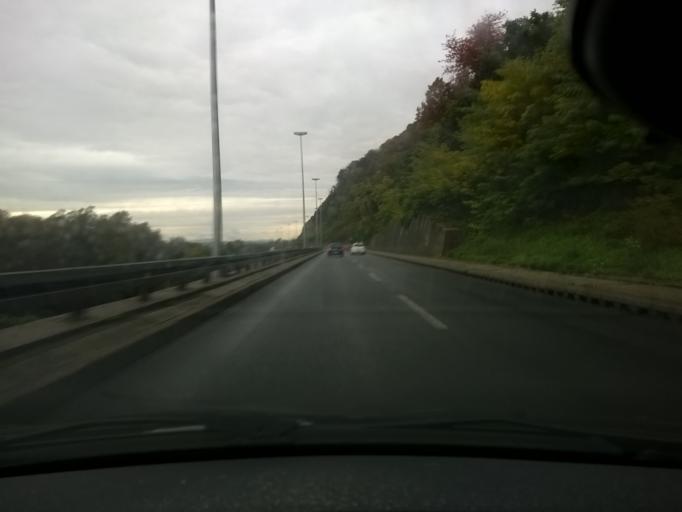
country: HR
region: Zagrebacka
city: Bestovje
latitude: 45.8264
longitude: 15.8263
